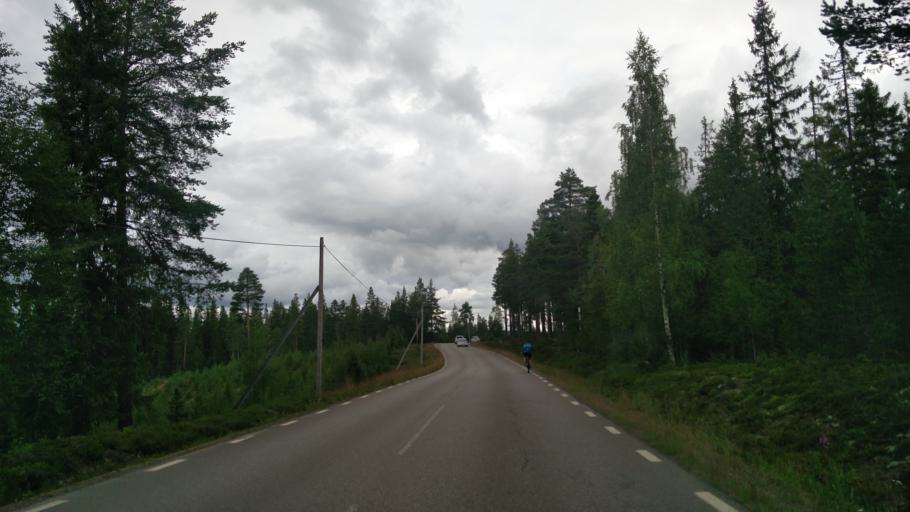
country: NO
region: Hedmark
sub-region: Trysil
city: Innbygda
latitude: 61.1611
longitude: 12.8220
